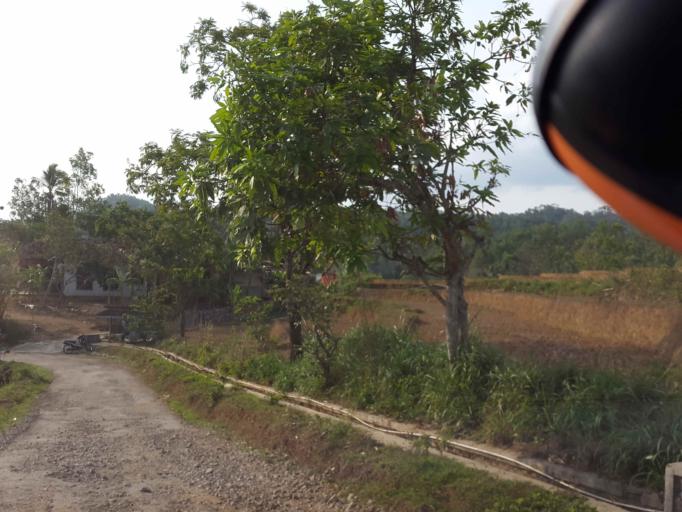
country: ID
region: East Java
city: Ploso
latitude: -8.0745
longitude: 111.0597
